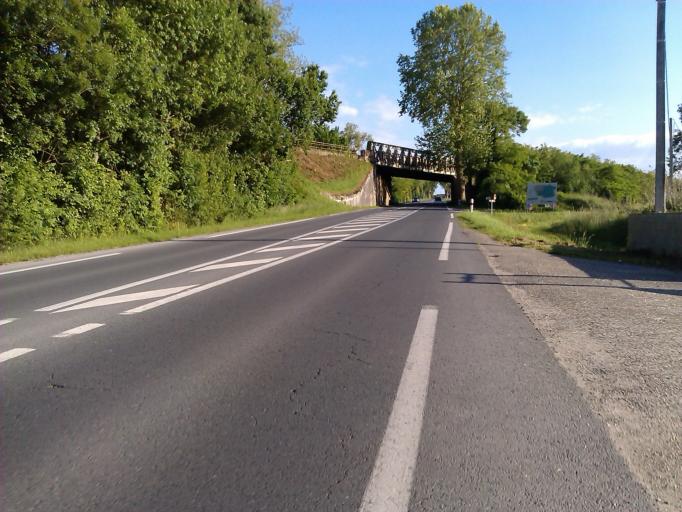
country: FR
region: Aquitaine
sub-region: Departement de la Gironde
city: Cubzac-les-Ponts
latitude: 44.9796
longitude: -0.4515
